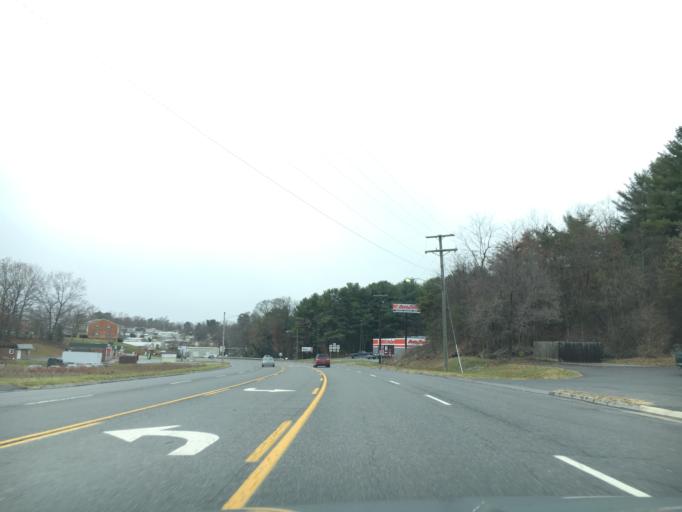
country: US
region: Virginia
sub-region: Montgomery County
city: Christiansburg
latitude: 37.1344
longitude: -80.3860
